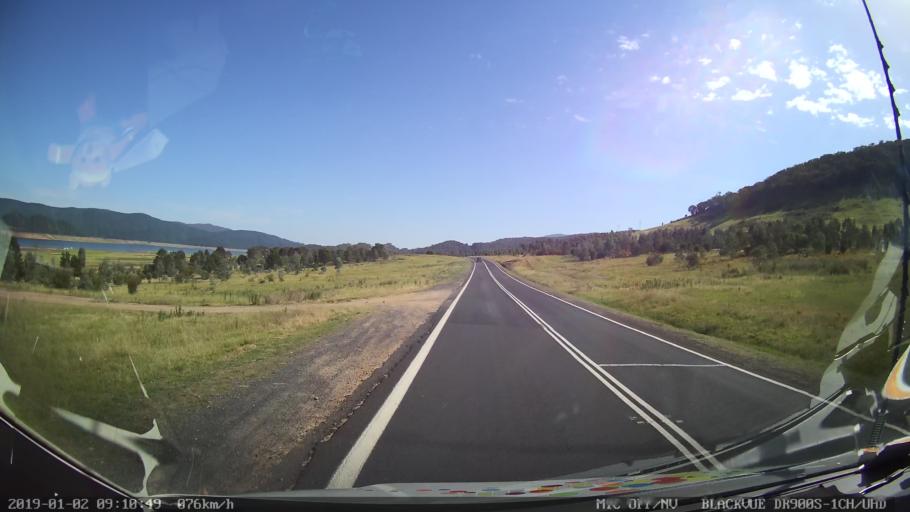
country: AU
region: New South Wales
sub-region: Tumut Shire
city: Tumut
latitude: -35.5180
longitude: 148.2685
